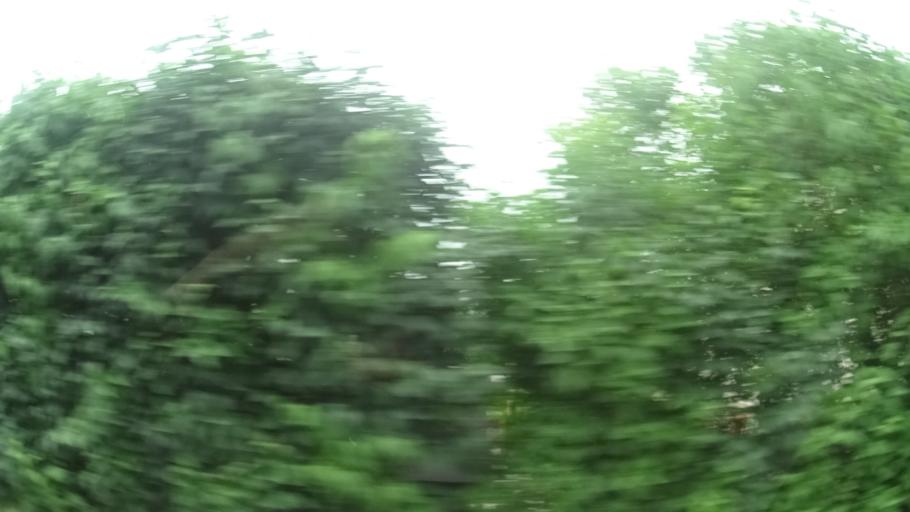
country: DE
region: Thuringia
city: Meiningen
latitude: 50.5838
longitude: 10.4062
